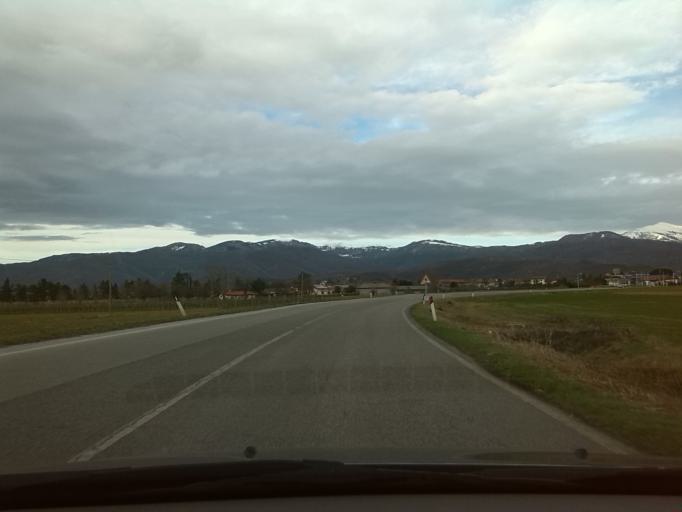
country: IT
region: Friuli Venezia Giulia
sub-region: Provincia di Udine
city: Cividale del Friuli
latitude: 46.0790
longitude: 13.4216
